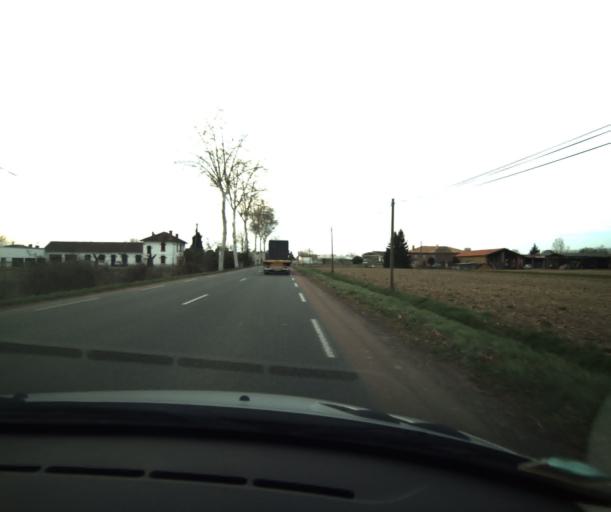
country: FR
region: Midi-Pyrenees
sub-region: Departement du Tarn-et-Garonne
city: Saint-Porquier
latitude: 44.0248
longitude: 1.1473
